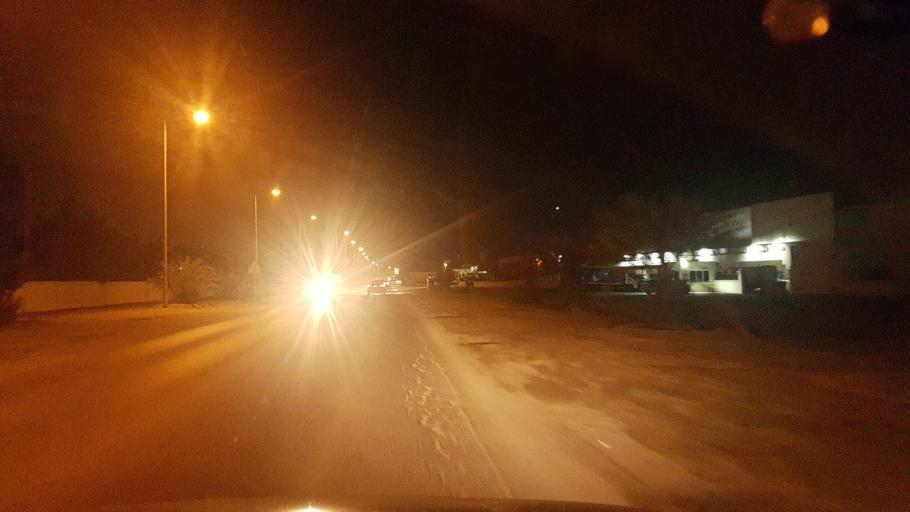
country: BH
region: Muharraq
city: Al Hadd
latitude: 26.2744
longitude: 50.6431
